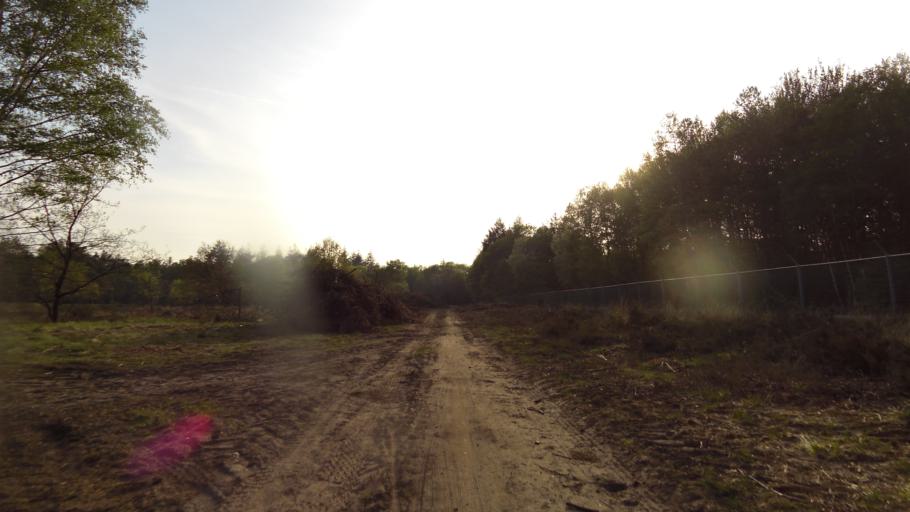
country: NL
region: Gelderland
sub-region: Gemeente Ede
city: Ede
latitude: 52.0641
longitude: 5.6965
